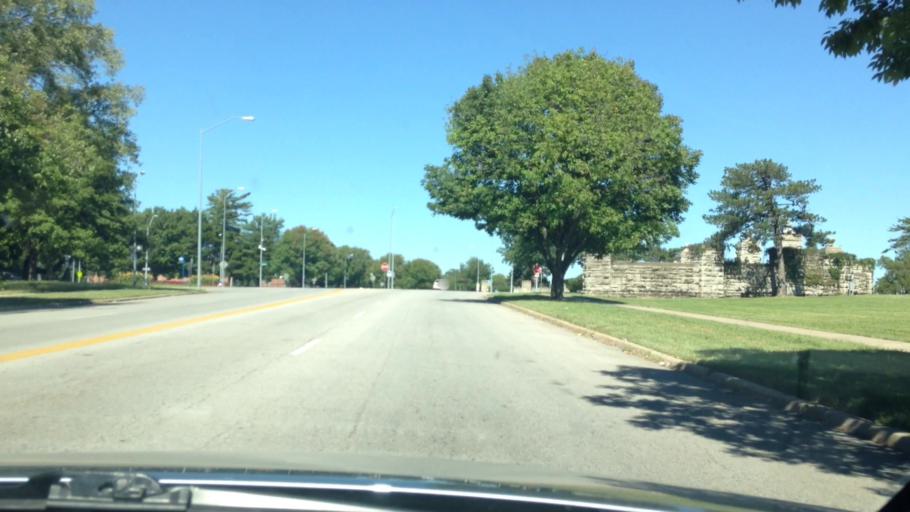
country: US
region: Kansas
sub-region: Johnson County
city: Mission Hills
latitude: 39.0062
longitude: -94.5425
